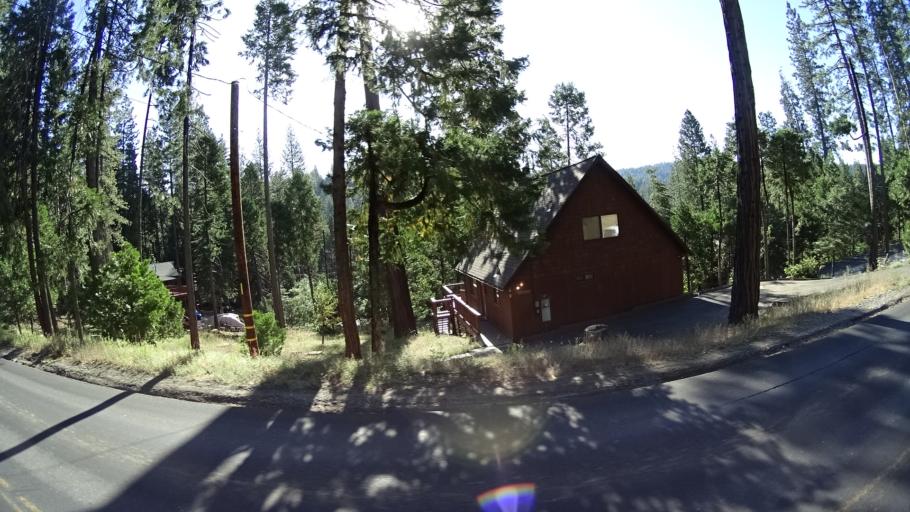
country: US
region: California
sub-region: Calaveras County
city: Arnold
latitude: 38.2641
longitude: -120.3331
